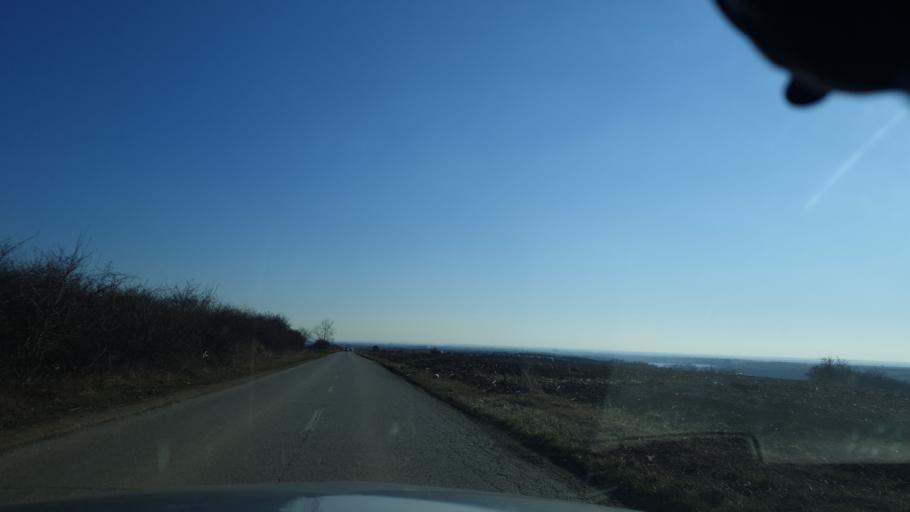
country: RS
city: Vrdnik
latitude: 45.0914
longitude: 19.8059
